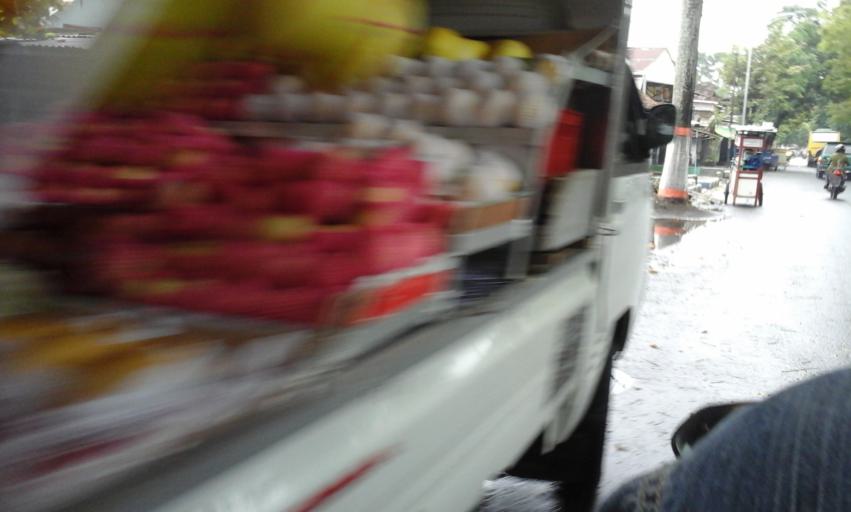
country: ID
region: East Java
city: Lumajang
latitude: -8.1391
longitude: 113.2300
